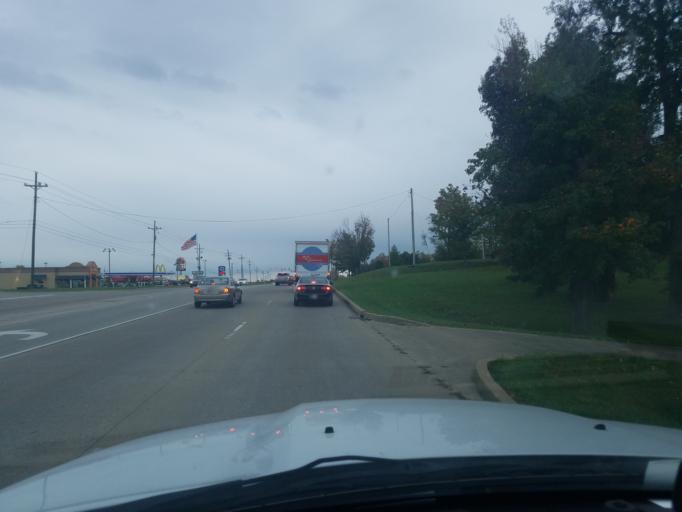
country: US
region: Indiana
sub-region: Floyd County
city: New Albany
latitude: 38.3417
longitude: -85.8171
